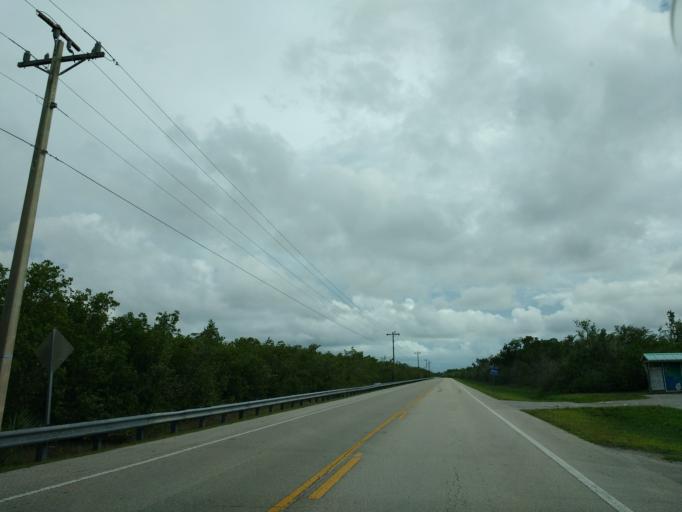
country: US
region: Florida
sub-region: Collier County
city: Marco
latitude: 25.8875
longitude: -81.3772
